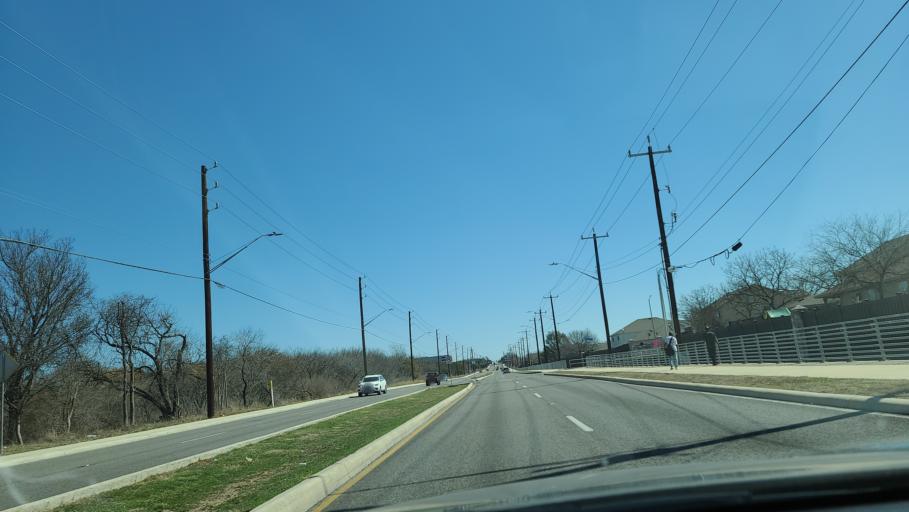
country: US
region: Texas
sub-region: Bexar County
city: Shavano Park
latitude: 29.5724
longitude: -98.6066
